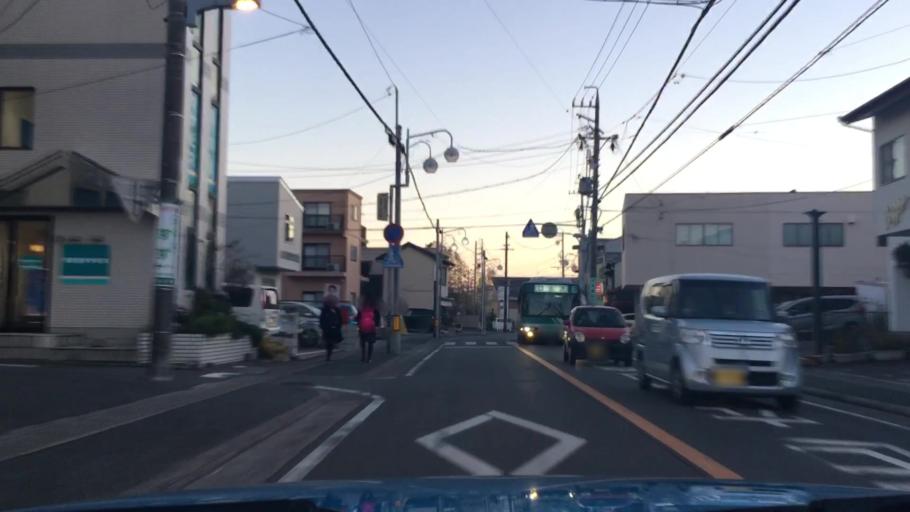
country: JP
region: Shizuoka
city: Hamamatsu
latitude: 34.7148
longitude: 137.7211
